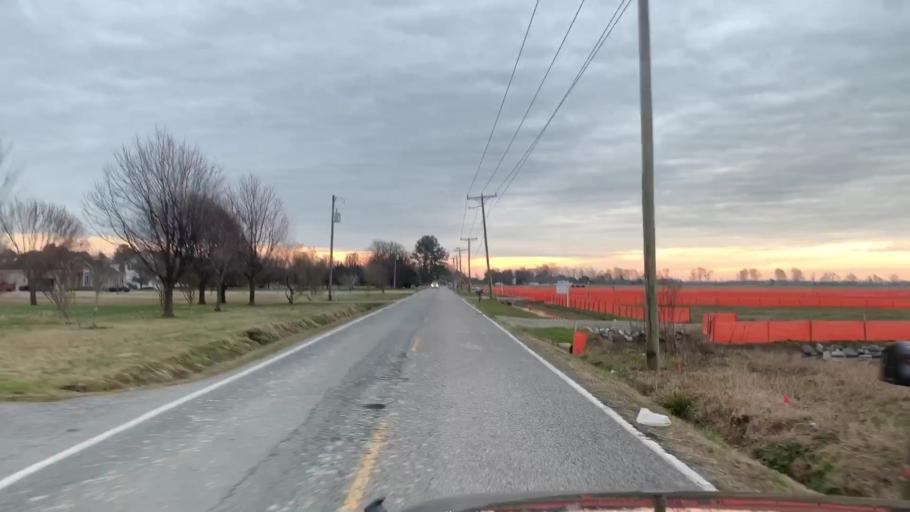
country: US
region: North Carolina
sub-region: Currituck County
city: Moyock
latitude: 36.6293
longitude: -76.1724
